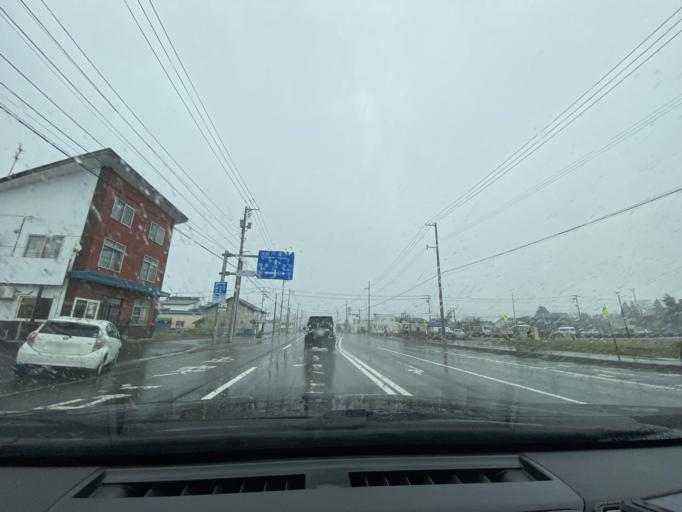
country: JP
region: Hokkaido
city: Takikawa
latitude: 43.6236
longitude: 141.9403
